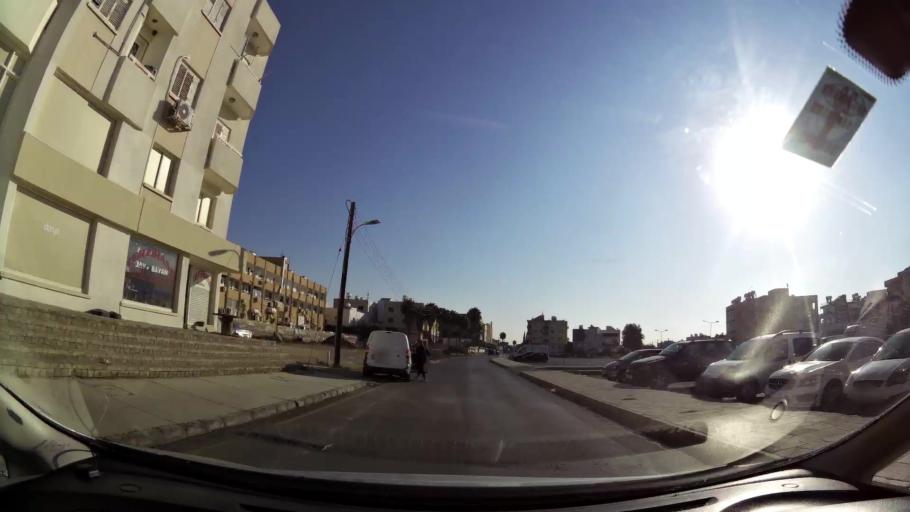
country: CY
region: Lefkosia
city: Nicosia
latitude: 35.2064
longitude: 33.3422
